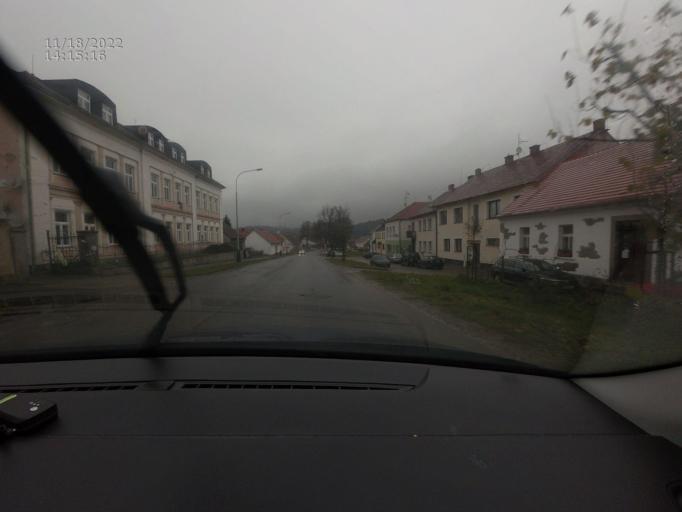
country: CZ
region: Jihocesky
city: Mirotice
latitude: 49.4272
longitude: 14.0368
